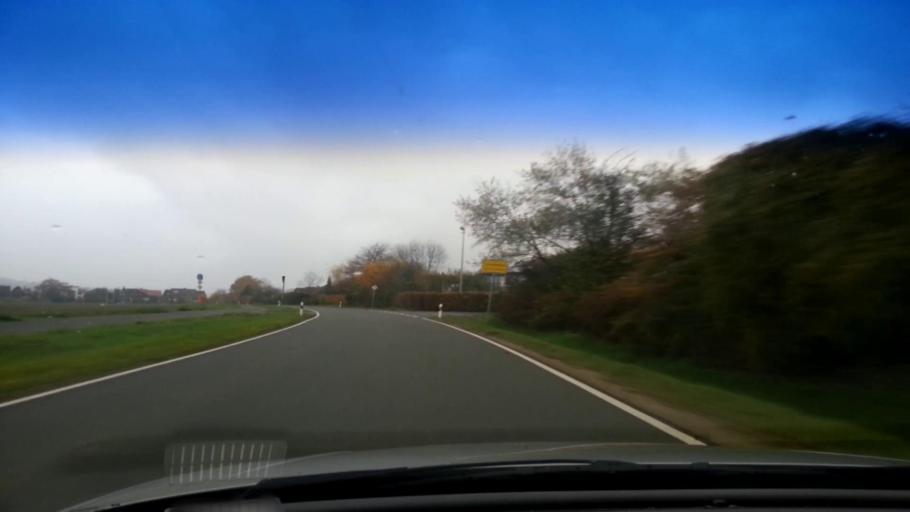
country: DE
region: Bavaria
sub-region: Upper Franconia
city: Litzendorf
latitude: 49.9076
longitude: 11.0162
